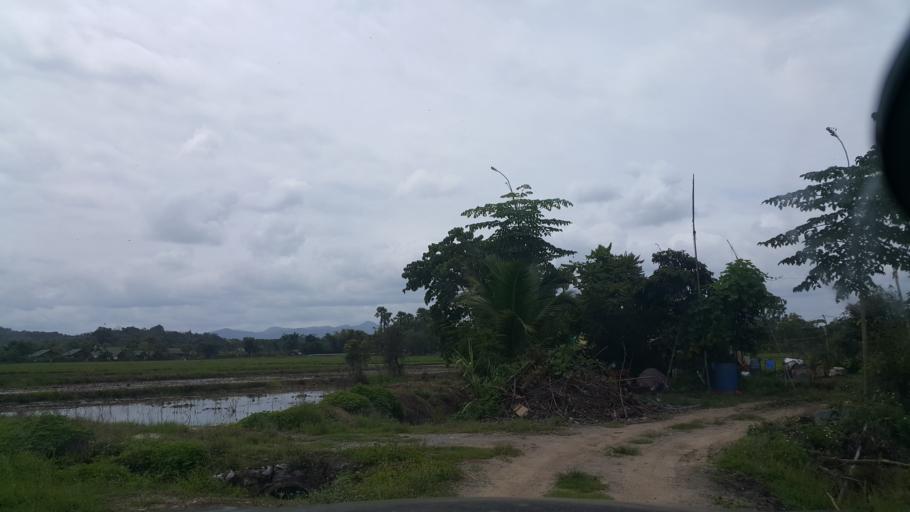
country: TH
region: Chiang Mai
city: San Kamphaeng
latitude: 18.7560
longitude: 99.1656
